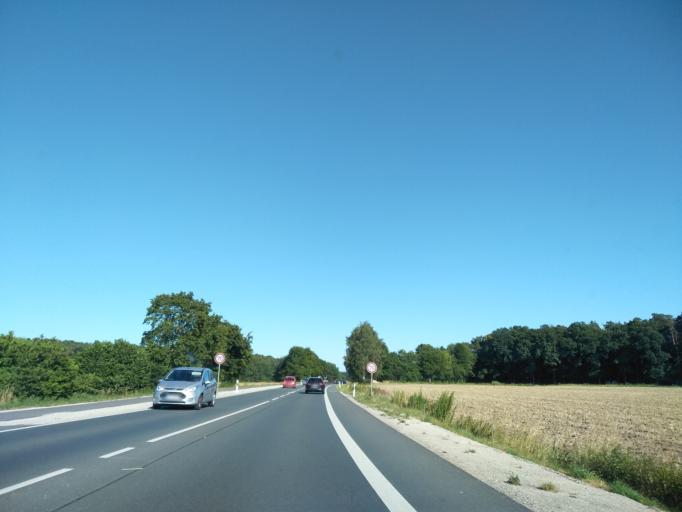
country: DE
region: Bavaria
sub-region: Regierungsbezirk Mittelfranken
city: Hessdorf
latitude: 49.6251
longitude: 10.9425
